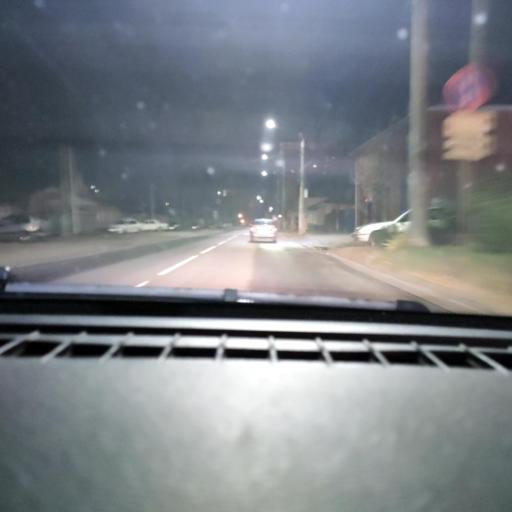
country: RU
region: Voronezj
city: Voronezh
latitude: 51.6483
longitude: 39.1850
